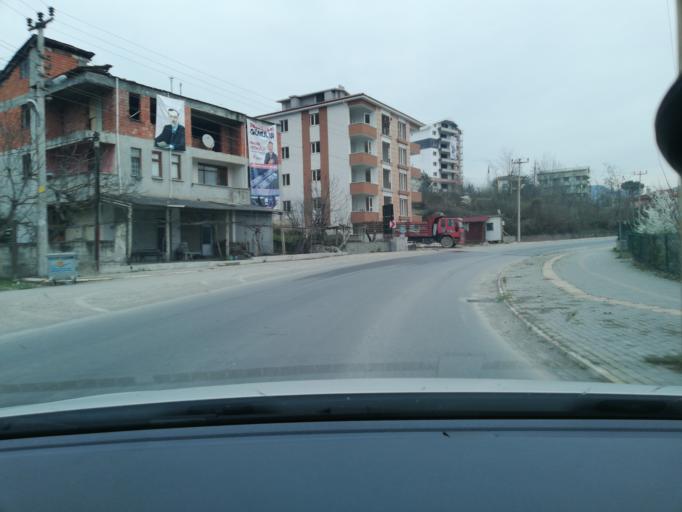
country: TR
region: Zonguldak
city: Gokcebey
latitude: 41.3101
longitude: 32.1311
